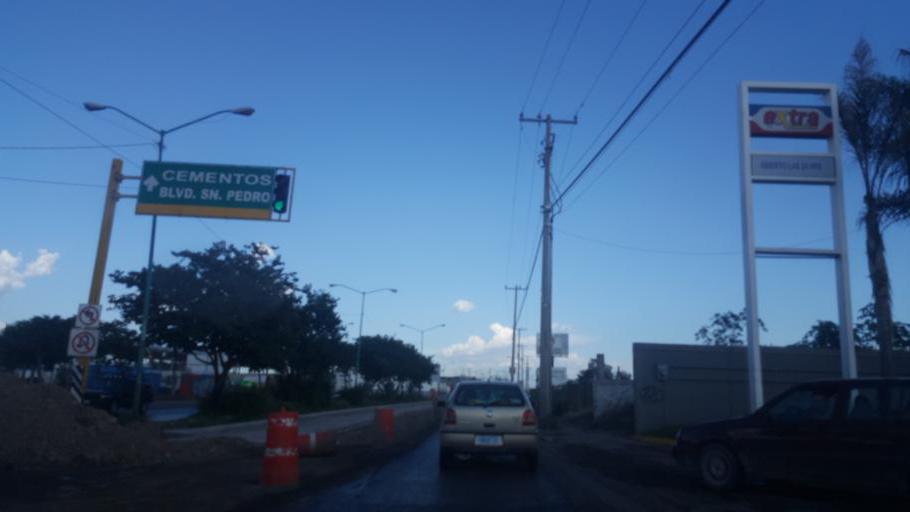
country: MX
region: Guanajuato
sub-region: Leon
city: San Jose de Duran (Los Troncoso)
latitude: 21.0911
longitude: -101.6782
